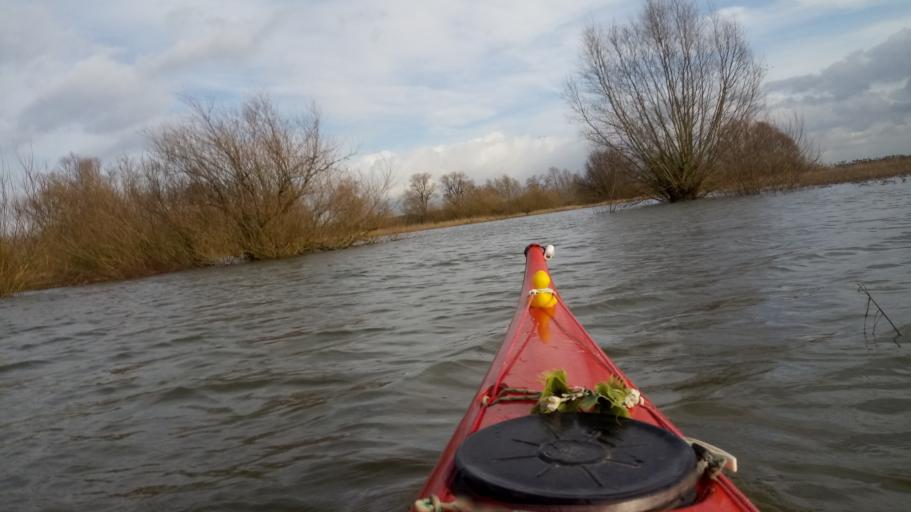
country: NL
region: Gelderland
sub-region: Gemeente Voorst
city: Voorst
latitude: 52.1872
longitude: 6.1631
